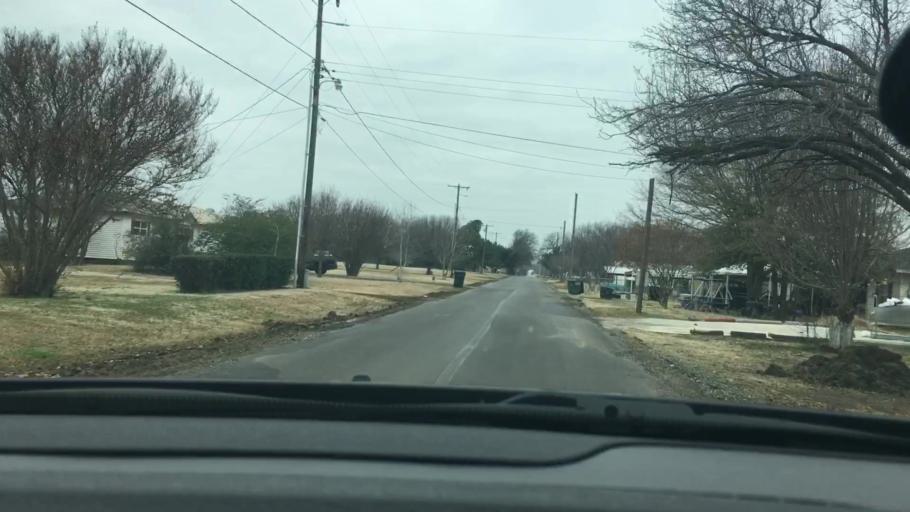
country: US
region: Oklahoma
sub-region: Carter County
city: Healdton
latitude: 34.2164
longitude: -97.4705
